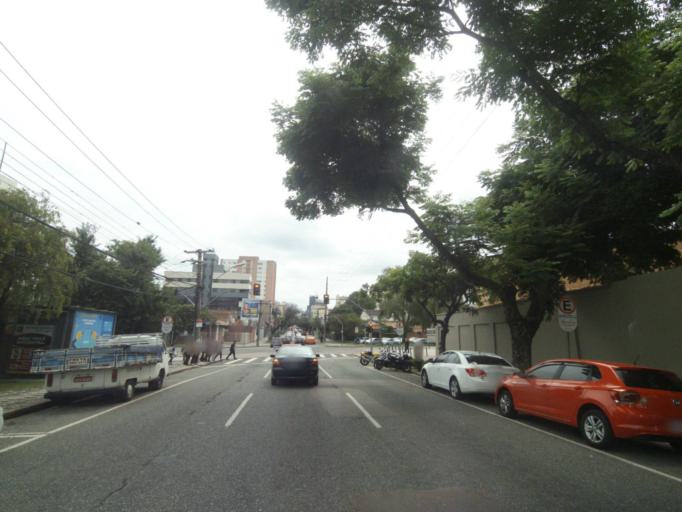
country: BR
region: Parana
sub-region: Curitiba
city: Curitiba
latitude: -25.4304
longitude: -49.2803
